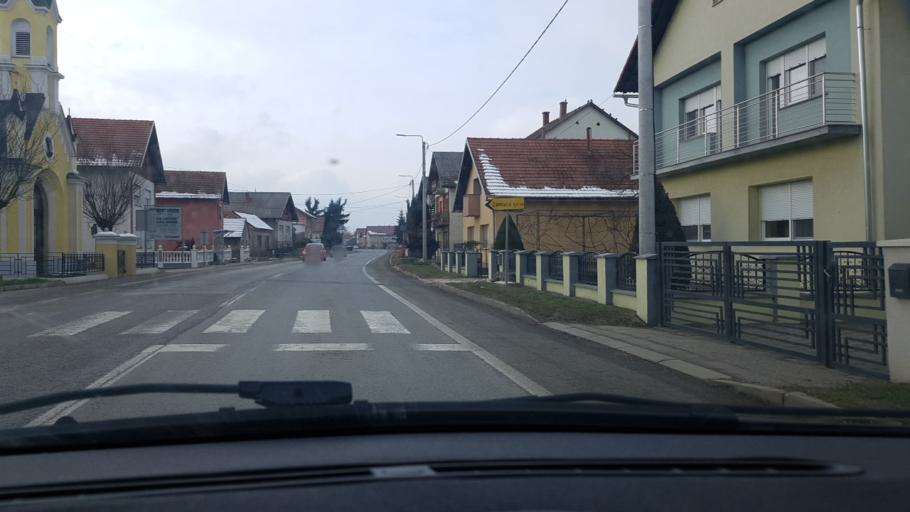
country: HR
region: Varazdinska
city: Nedeljanec
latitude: 46.2860
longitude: 16.2684
